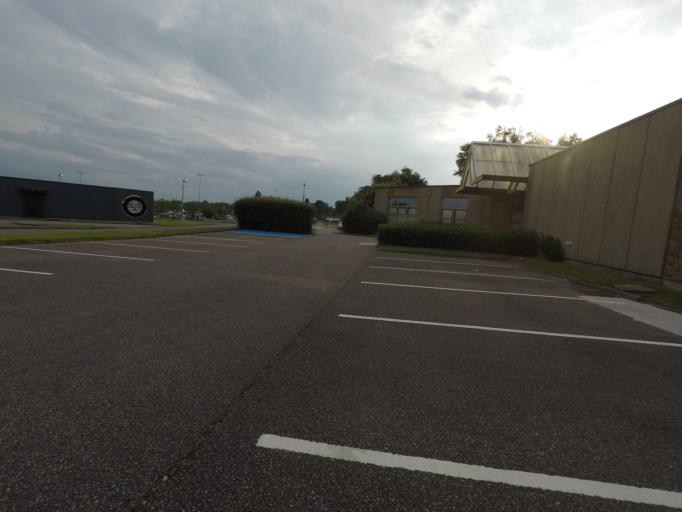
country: FR
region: Haute-Normandie
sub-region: Departement de la Seine-Maritime
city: Mont-Saint-Aignan
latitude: 49.4727
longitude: 1.0970
